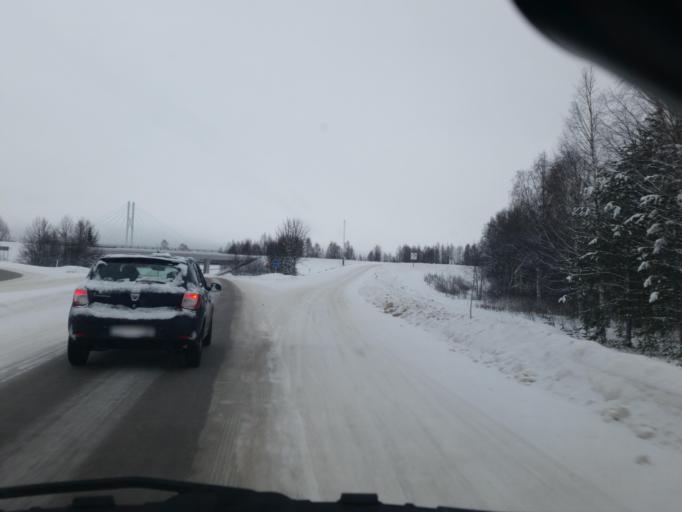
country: SE
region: Norrbotten
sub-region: Pitea Kommun
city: Bergsviken
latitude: 65.3122
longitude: 21.4036
